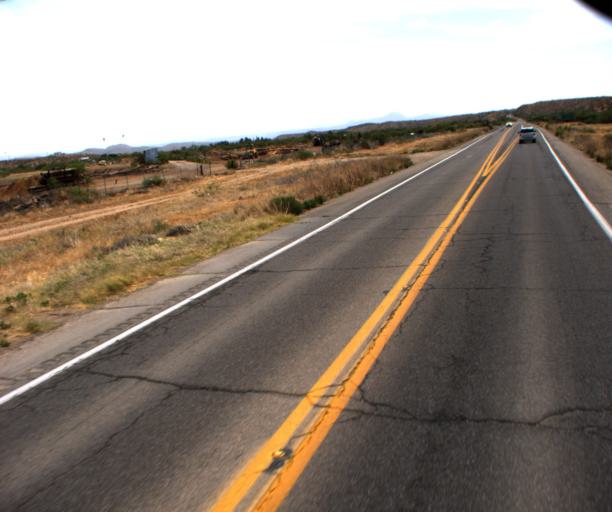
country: US
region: Arizona
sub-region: Gila County
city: Globe
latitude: 33.3527
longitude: -110.6537
